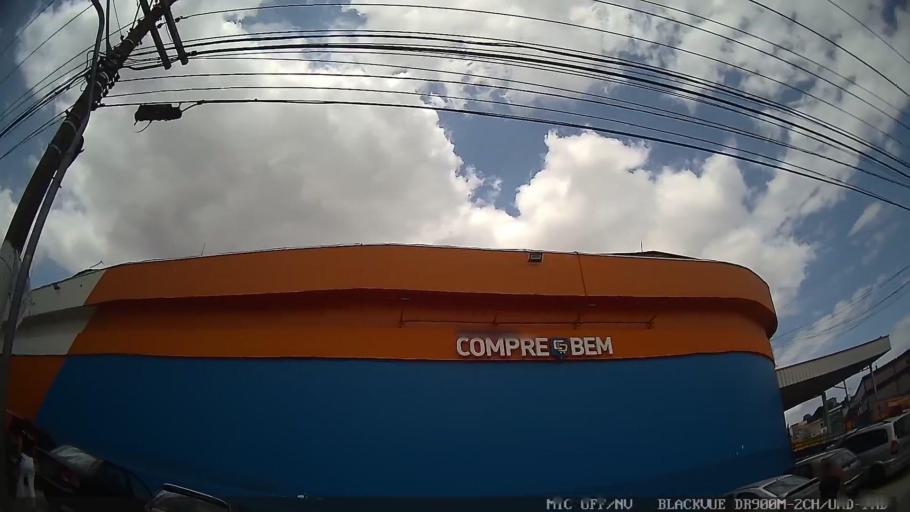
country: BR
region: Sao Paulo
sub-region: Ferraz De Vasconcelos
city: Ferraz de Vasconcelos
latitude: -23.5351
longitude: -46.4565
